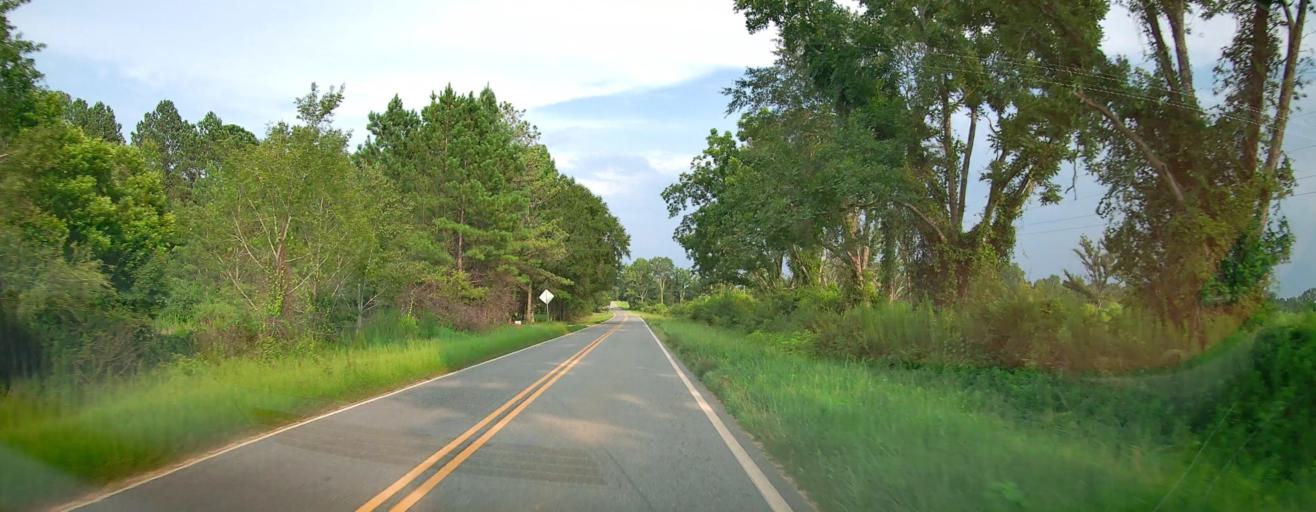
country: US
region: Georgia
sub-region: Laurens County
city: Dublin
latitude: 32.4847
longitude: -82.9726
